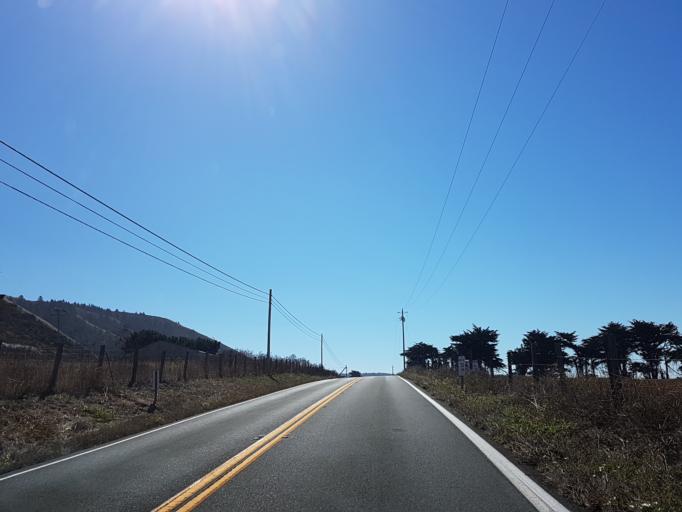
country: US
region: California
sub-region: Mendocino County
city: Boonville
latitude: 39.0828
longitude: -123.6975
